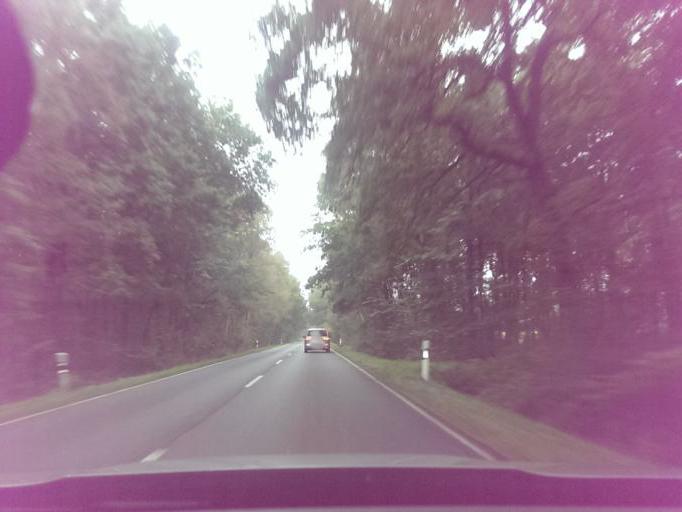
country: DE
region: Lower Saxony
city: Garbsen-Mitte
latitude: 52.4820
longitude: 9.6370
